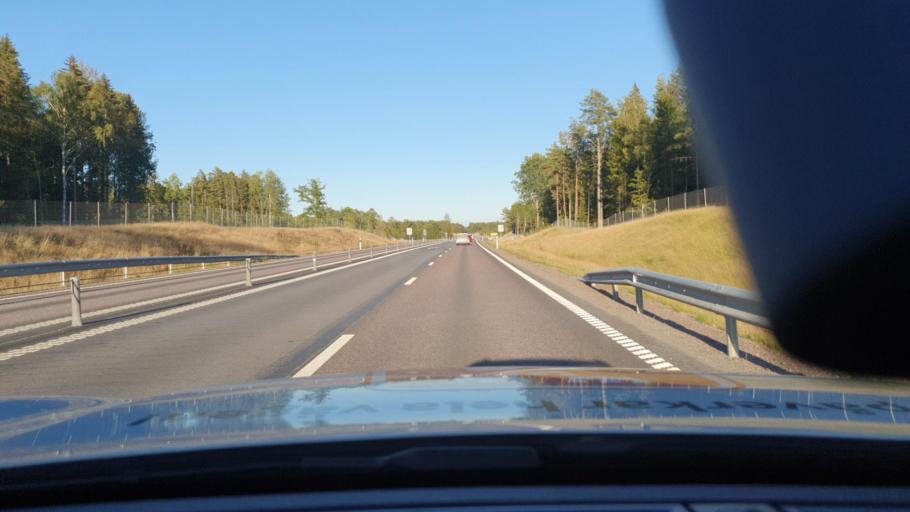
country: SE
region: OEstergoetland
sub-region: Motala Kommun
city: Ryd
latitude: 58.5869
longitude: 15.1381
